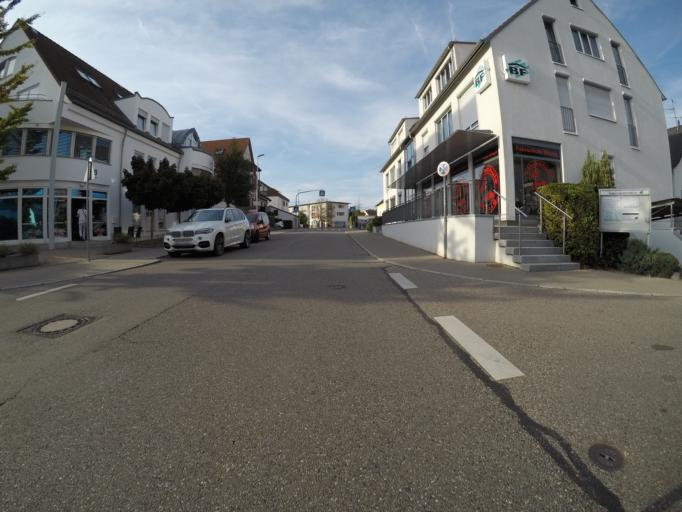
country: DE
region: Baden-Wuerttemberg
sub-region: Regierungsbezirk Stuttgart
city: Esslingen
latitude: 48.7151
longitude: 9.2972
